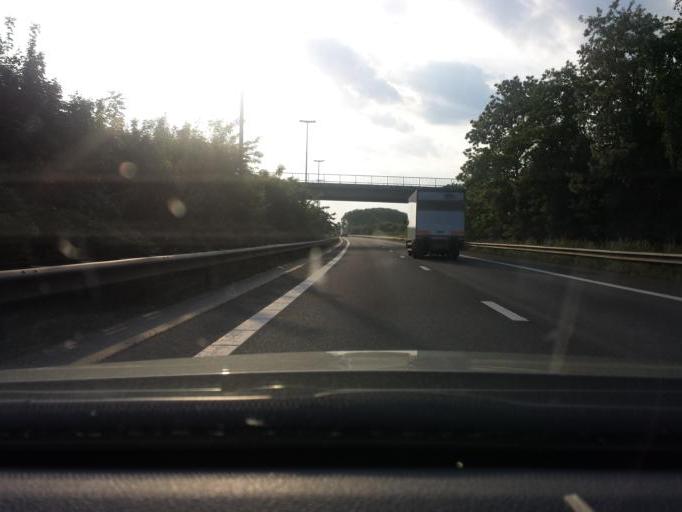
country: BE
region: Flanders
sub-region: Provincie Limburg
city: Diepenbeek
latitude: 50.8882
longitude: 5.4412
